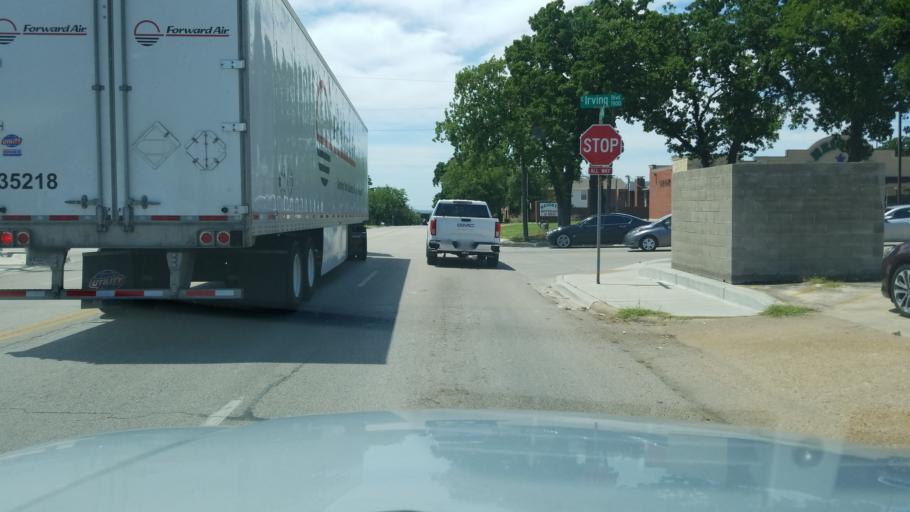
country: US
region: Texas
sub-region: Dallas County
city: Irving
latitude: 32.8081
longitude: -96.9257
